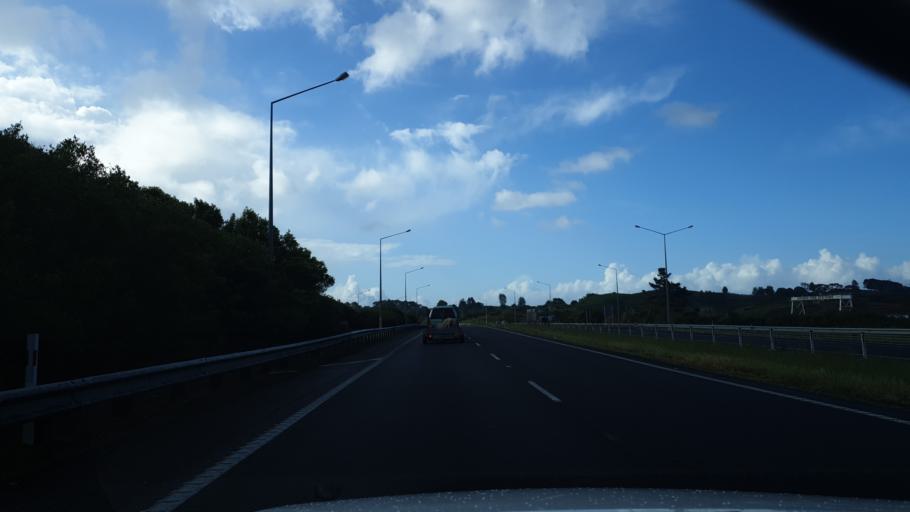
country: NZ
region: Auckland
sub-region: Auckland
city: Pukekohe East
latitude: -37.2482
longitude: 175.0282
